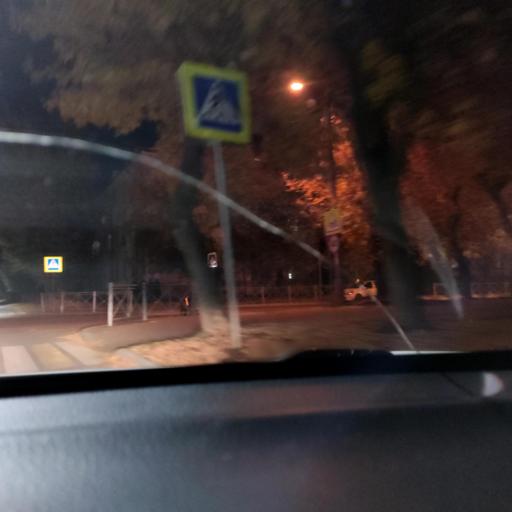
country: RU
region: Tatarstan
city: Vysokaya Gora
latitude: 55.8682
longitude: 49.2231
